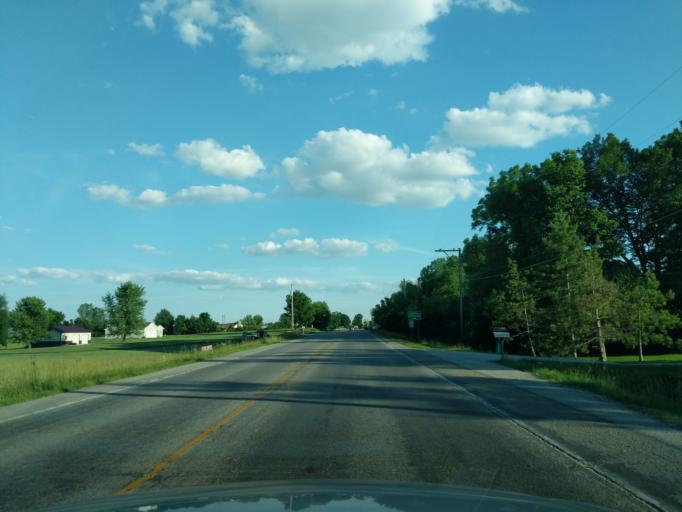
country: US
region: Indiana
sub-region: Huntington County
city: Huntington
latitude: 40.8616
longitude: -85.4705
